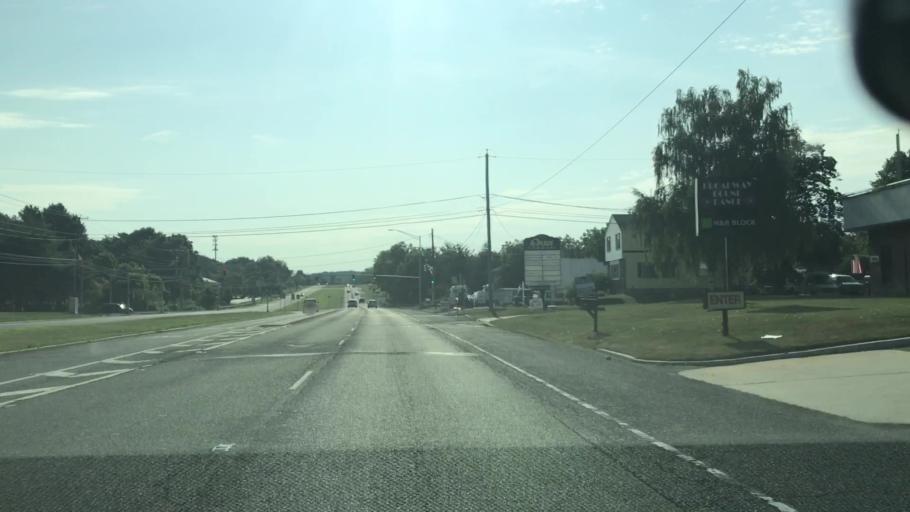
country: US
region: New Jersey
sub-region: Hunterdon County
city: Lebanon
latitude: 40.6438
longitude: -74.8275
